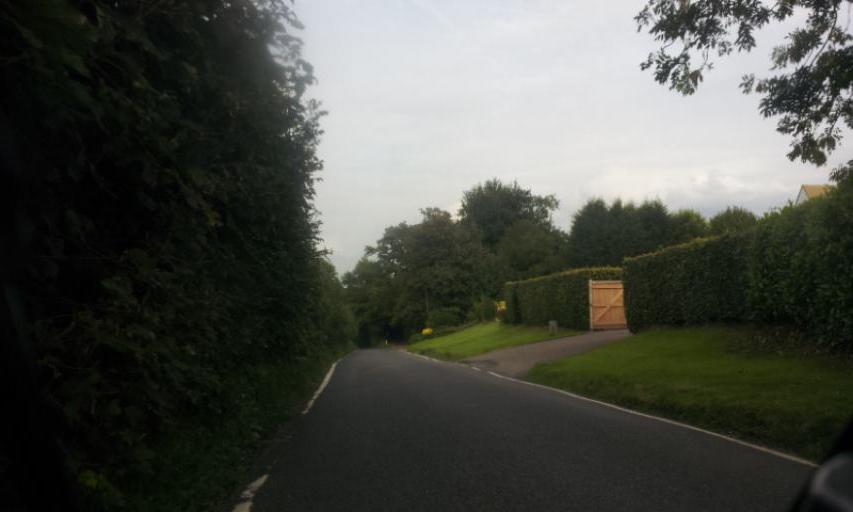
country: GB
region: England
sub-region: Kent
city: Tonbridge
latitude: 51.1669
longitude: 0.2531
